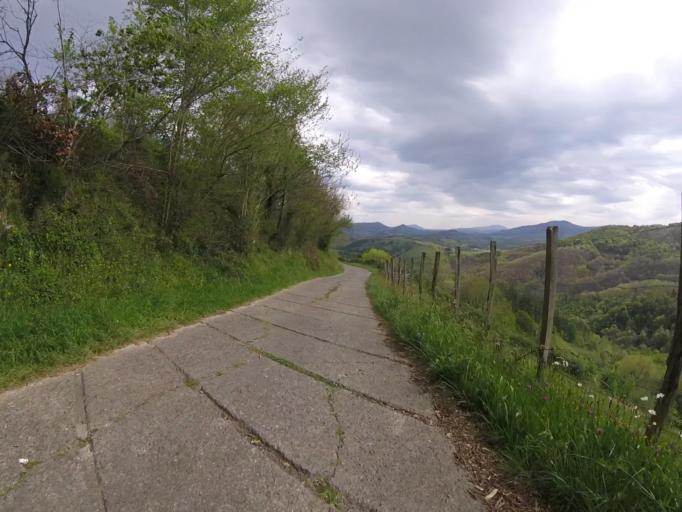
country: ES
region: Basque Country
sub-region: Provincia de Guipuzcoa
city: Zarautz
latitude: 43.2544
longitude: -2.1779
